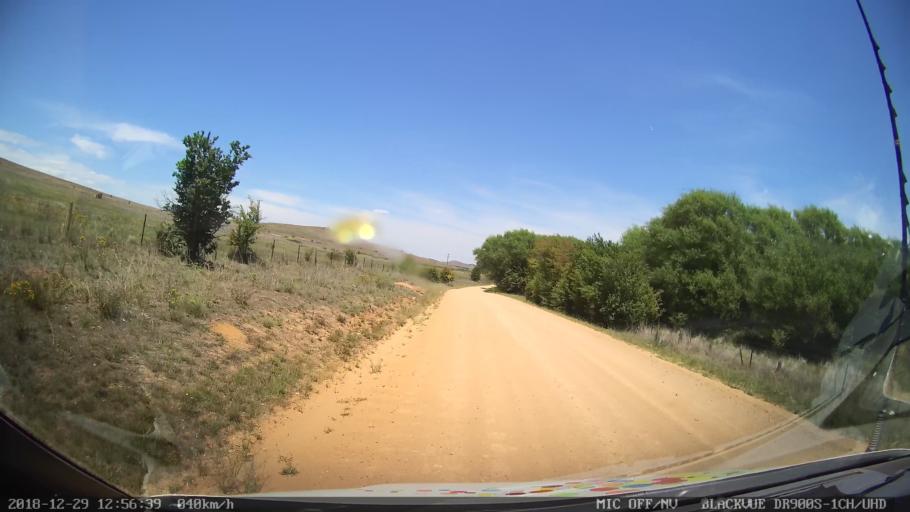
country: AU
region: Australian Capital Territory
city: Macarthur
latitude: -35.7028
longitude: 149.1810
